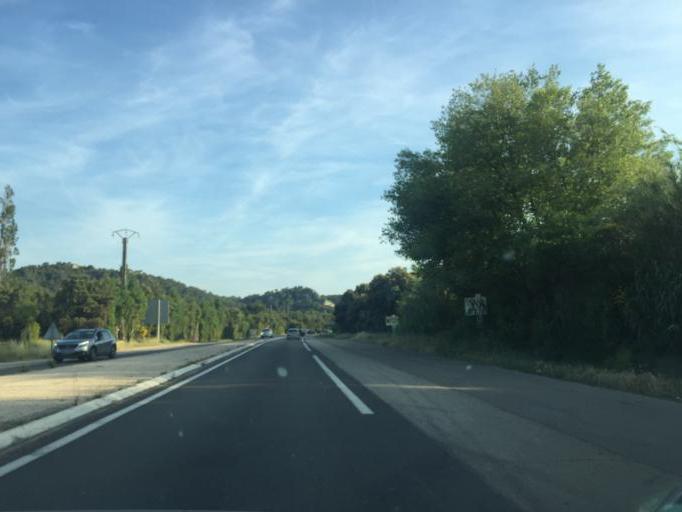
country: FR
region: Languedoc-Roussillon
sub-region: Departement du Gard
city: Les Angles
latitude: 43.9758
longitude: 4.7475
